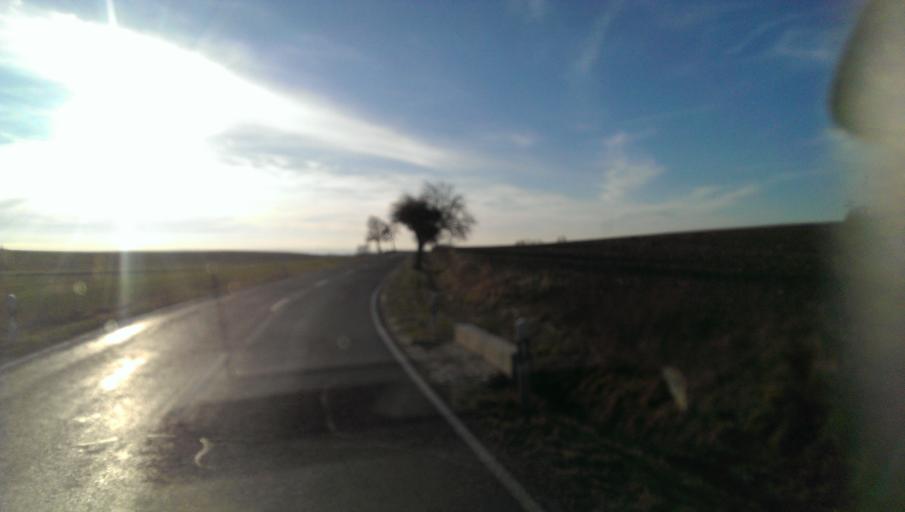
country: DE
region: Saxony-Anhalt
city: Ummendorf
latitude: 52.1037
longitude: 11.1792
